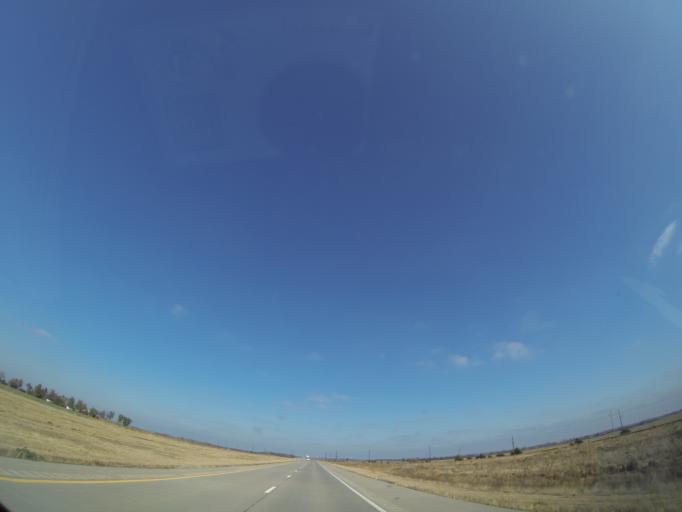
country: US
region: Kansas
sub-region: McPherson County
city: Inman
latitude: 38.1906
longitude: -97.8102
